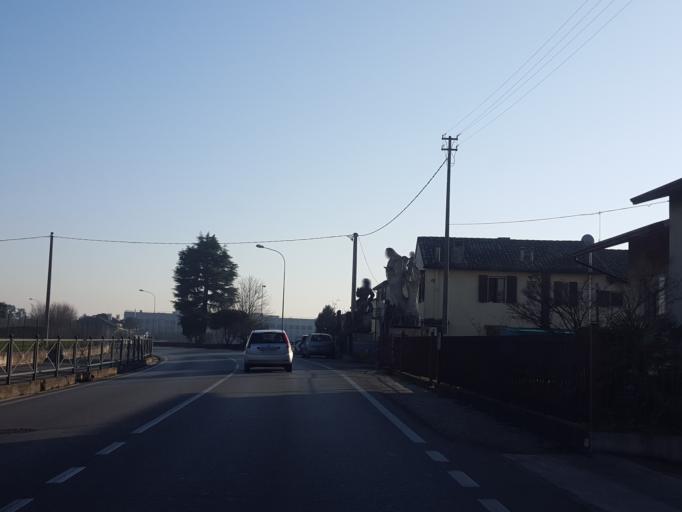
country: IT
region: Veneto
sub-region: Provincia di Vicenza
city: Torri di Quartesolo
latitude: 45.5259
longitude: 11.6333
